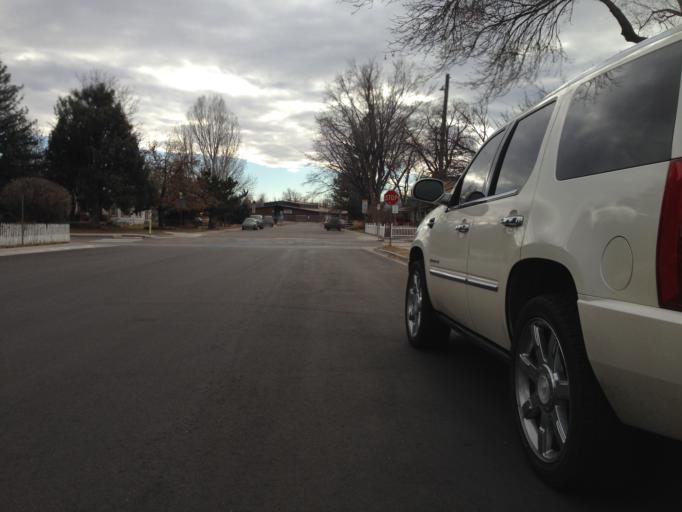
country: US
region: Colorado
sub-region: Boulder County
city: Louisville
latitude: 39.9772
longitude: -105.1381
